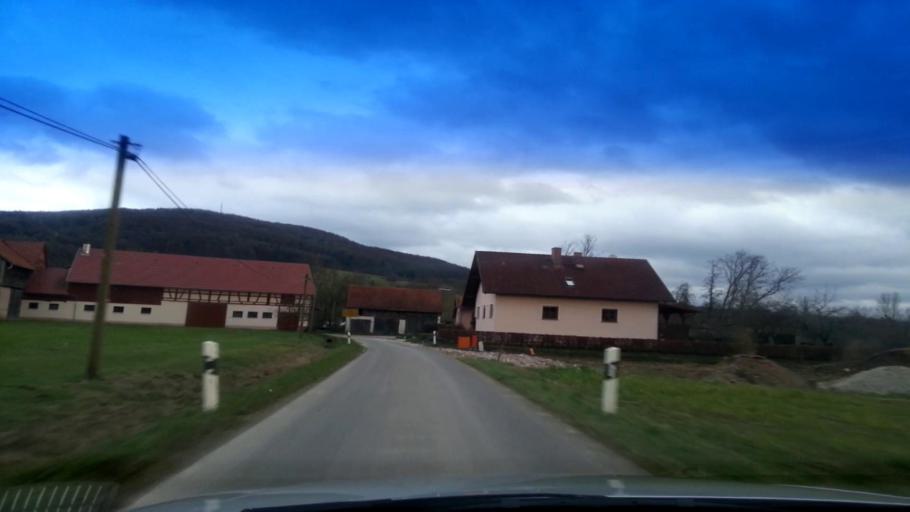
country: DE
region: Bavaria
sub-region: Upper Franconia
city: Schesslitz
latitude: 49.9976
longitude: 11.0537
